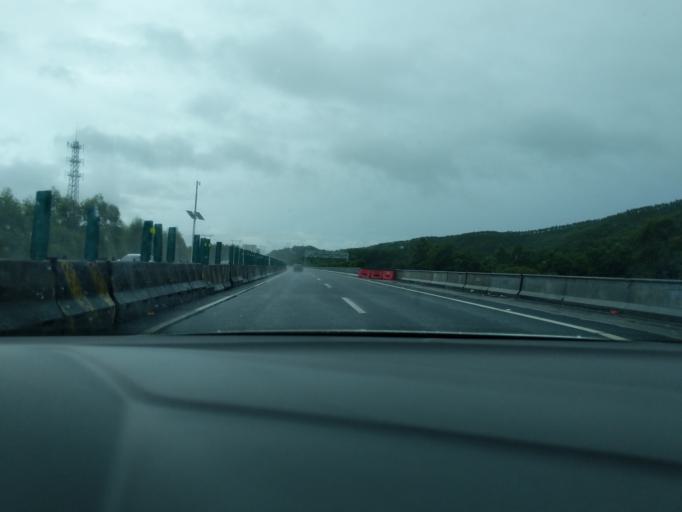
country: CN
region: Guangdong
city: Liangxi
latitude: 22.2726
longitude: 112.3297
